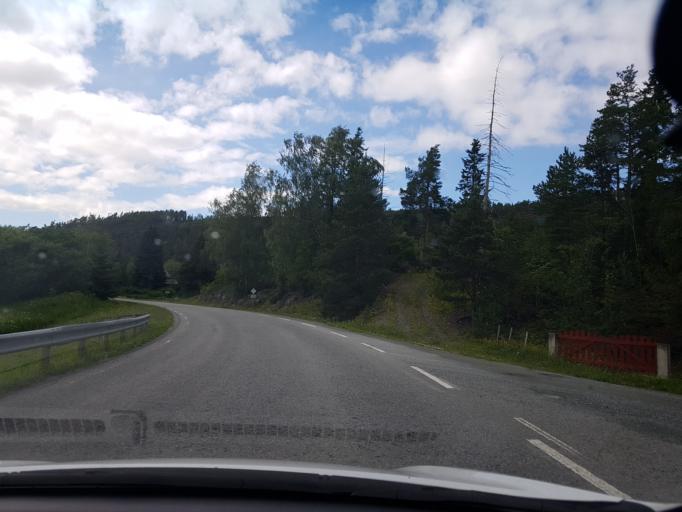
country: NO
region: Nord-Trondelag
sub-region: Stjordal
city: Stjordalshalsen
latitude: 63.6136
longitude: 10.9356
